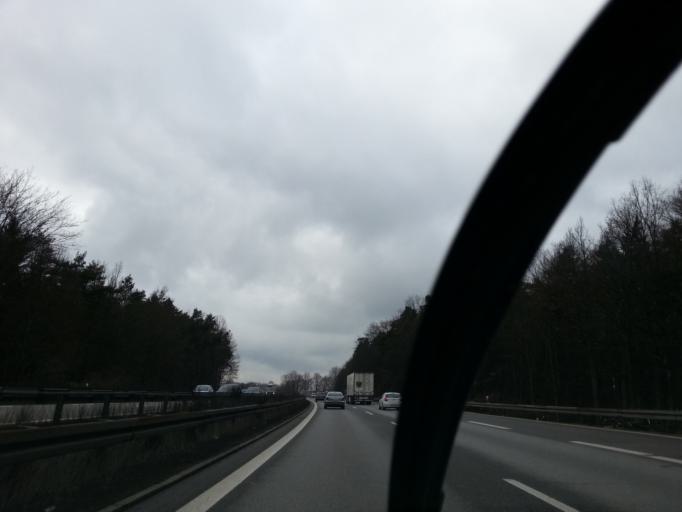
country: DE
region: Bavaria
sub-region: Upper Palatinate
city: Sinzing
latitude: 49.0073
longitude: 11.9977
